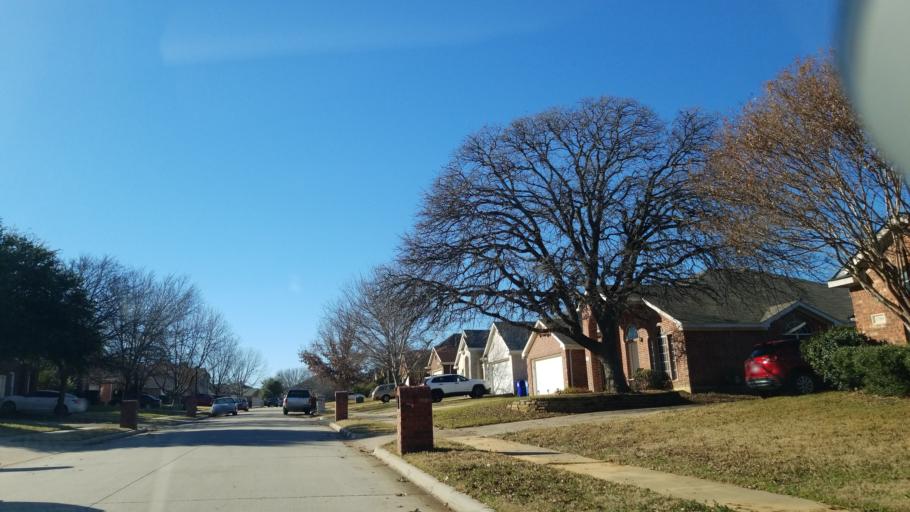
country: US
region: Texas
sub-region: Denton County
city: Corinth
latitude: 33.1392
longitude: -97.0826
